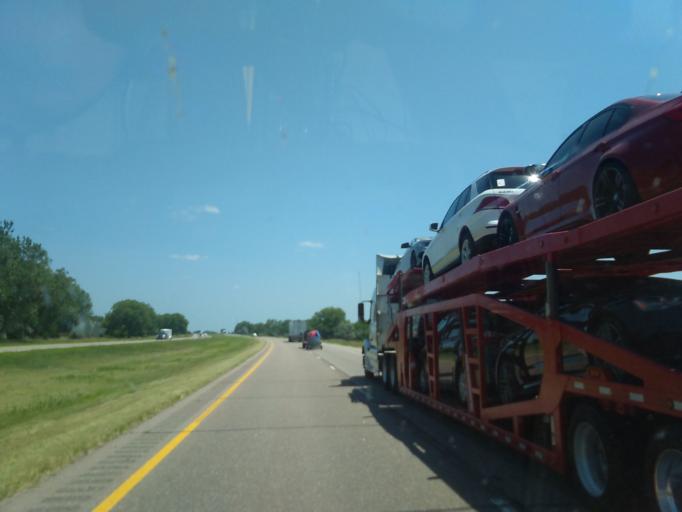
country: US
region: Nebraska
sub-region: Dawson County
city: Gothenburg
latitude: 40.8873
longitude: -100.0990
